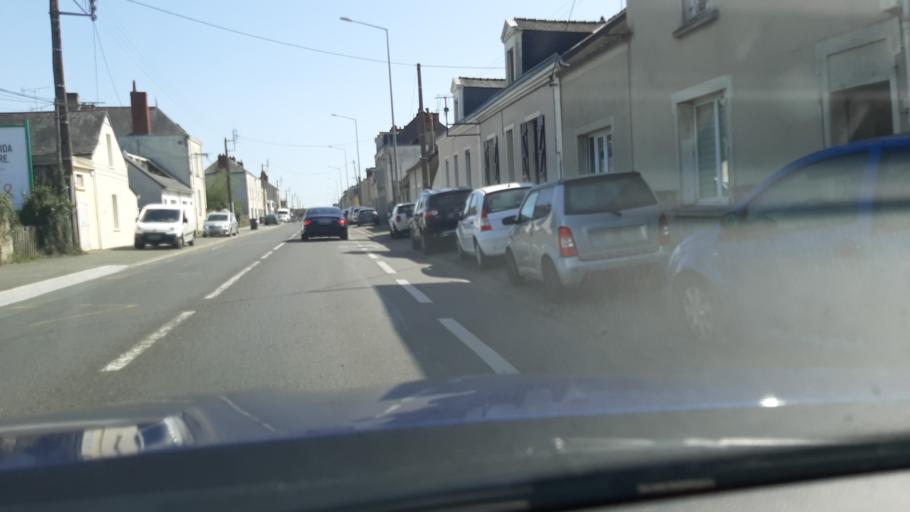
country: FR
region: Pays de la Loire
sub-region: Departement de Maine-et-Loire
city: Les Ponts-de-Ce
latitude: 47.4512
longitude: -0.5199
